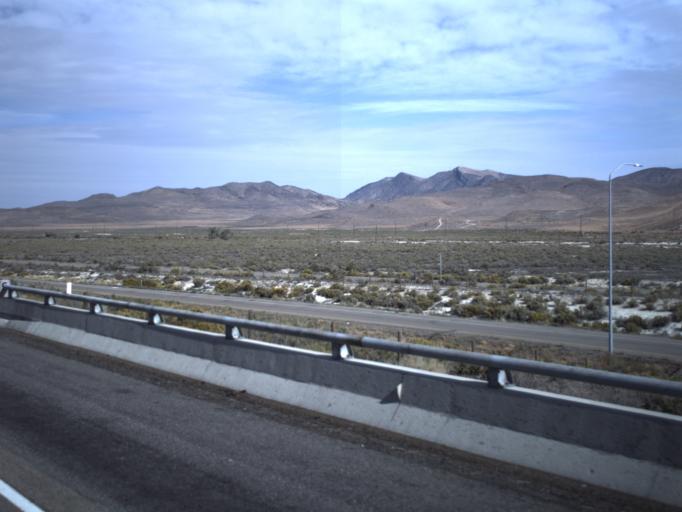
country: US
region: Utah
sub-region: Tooele County
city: Grantsville
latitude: 40.7629
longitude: -112.7812
